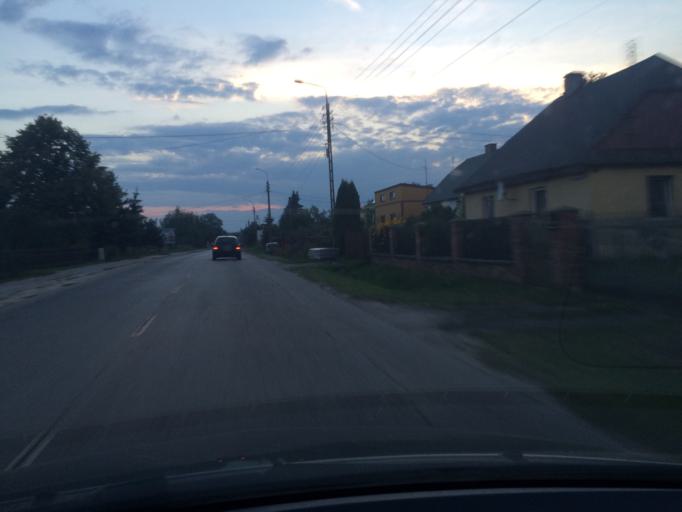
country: PL
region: Swietokrzyskie
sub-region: Powiat skarzyski
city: Suchedniow
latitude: 51.0455
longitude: 20.8710
